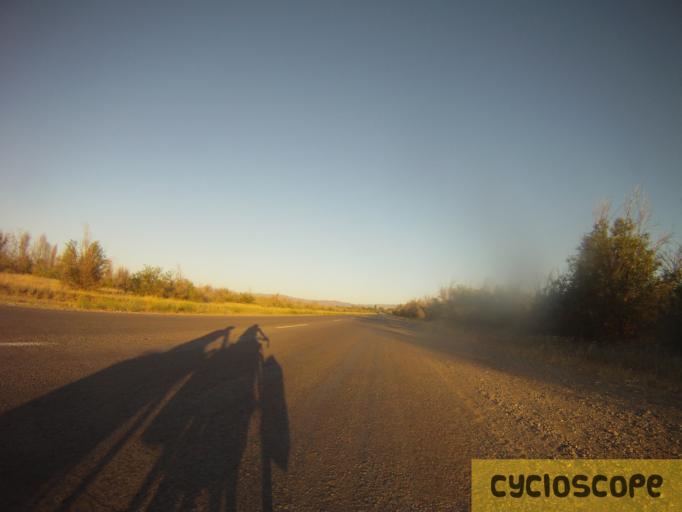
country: KZ
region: Almaty Oblysy
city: Turgen'
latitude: 43.5883
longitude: 78.3337
